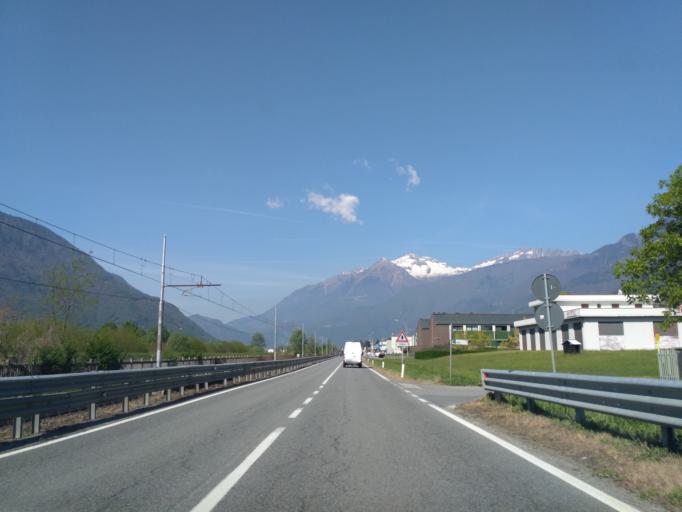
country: IT
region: Lombardy
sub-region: Provincia di Sondrio
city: Cedrasco
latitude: 46.1591
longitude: 9.7594
